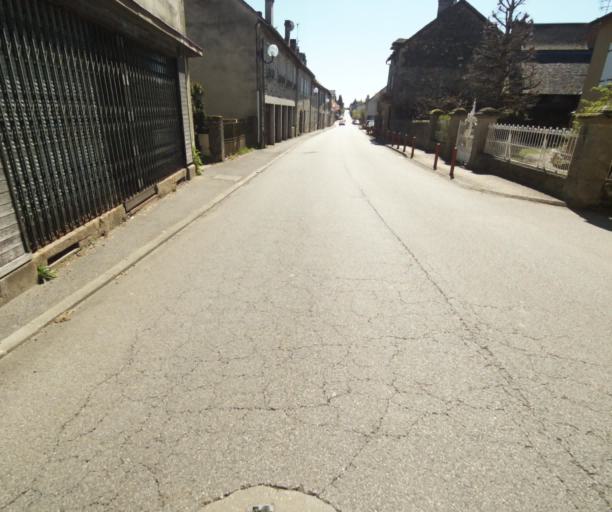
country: FR
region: Limousin
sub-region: Departement de la Correze
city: Chamboulive
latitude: 45.4320
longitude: 1.7046
